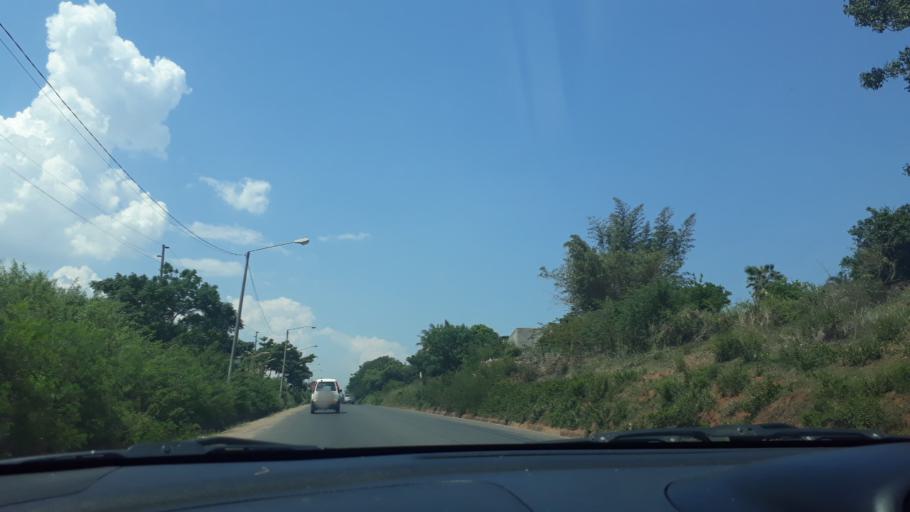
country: MZ
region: Maputo
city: Matola
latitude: -25.9626
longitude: 32.4480
